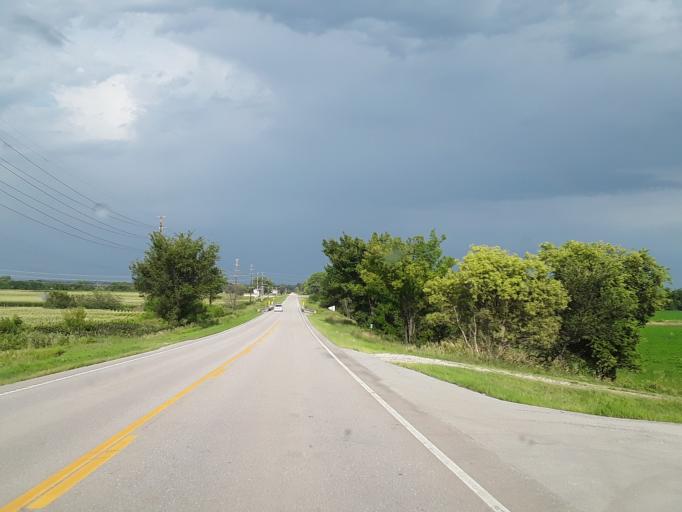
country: US
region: Nebraska
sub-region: Saunders County
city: Ashland
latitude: 41.0886
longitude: -96.3828
